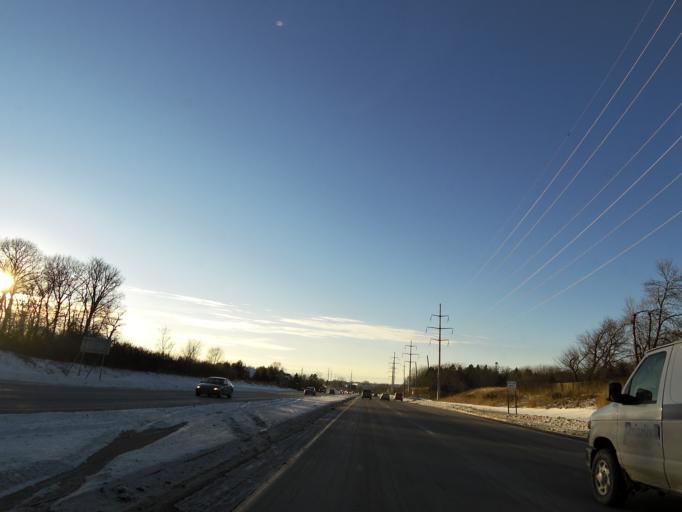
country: US
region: Minnesota
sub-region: Hennepin County
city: Eden Prairie
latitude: 44.8629
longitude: -93.4952
